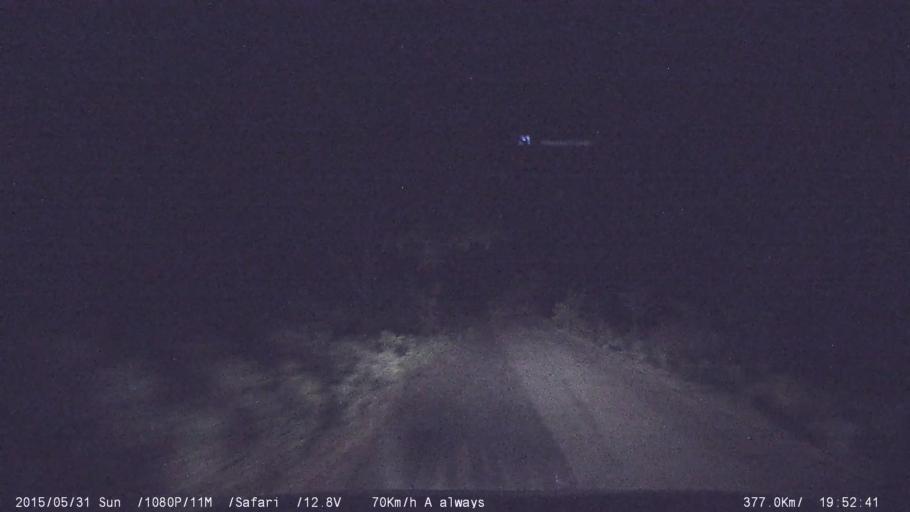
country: IN
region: Karnataka
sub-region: Mandya
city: Malavalli
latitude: 12.3373
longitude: 77.0761
